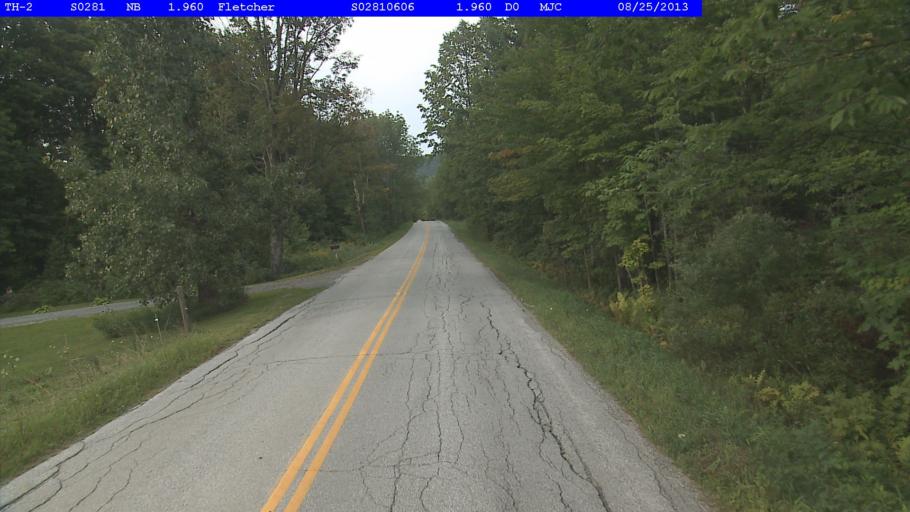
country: US
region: Vermont
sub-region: Franklin County
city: Saint Albans
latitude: 44.7025
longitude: -72.9376
